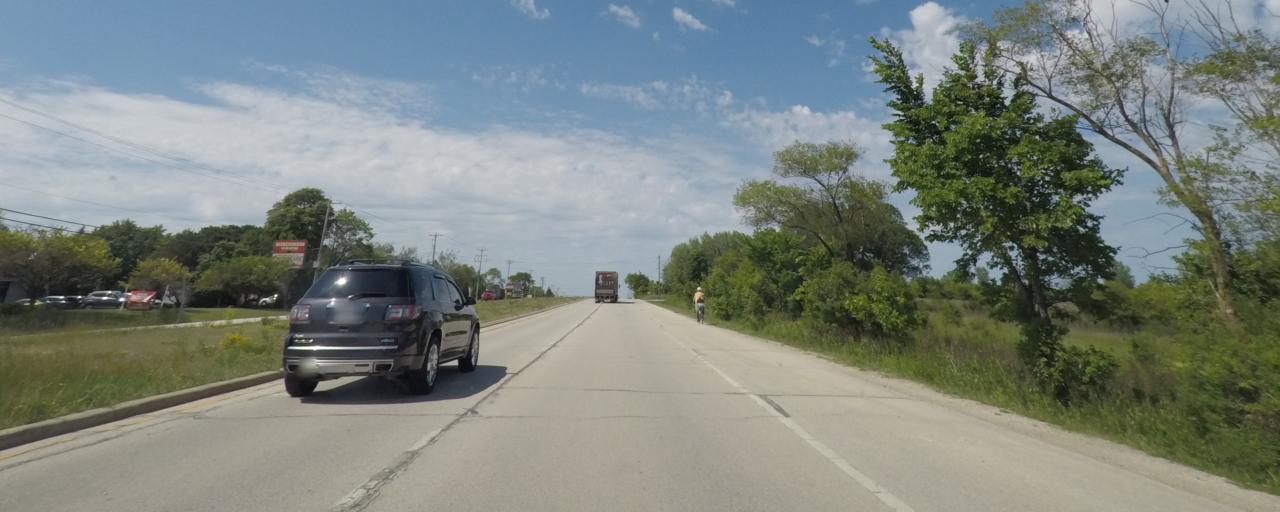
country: US
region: Wisconsin
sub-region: Milwaukee County
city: Greendale
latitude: 42.8954
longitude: -87.9505
